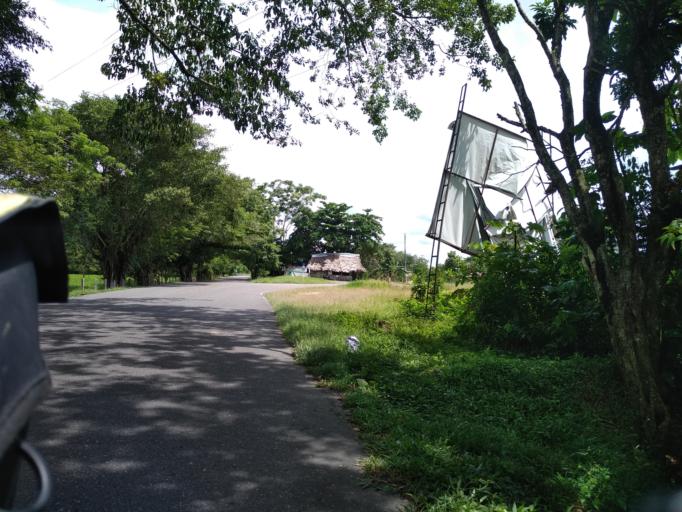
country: CO
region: Santander
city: Puerto Parra
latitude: 6.5215
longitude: -74.0813
